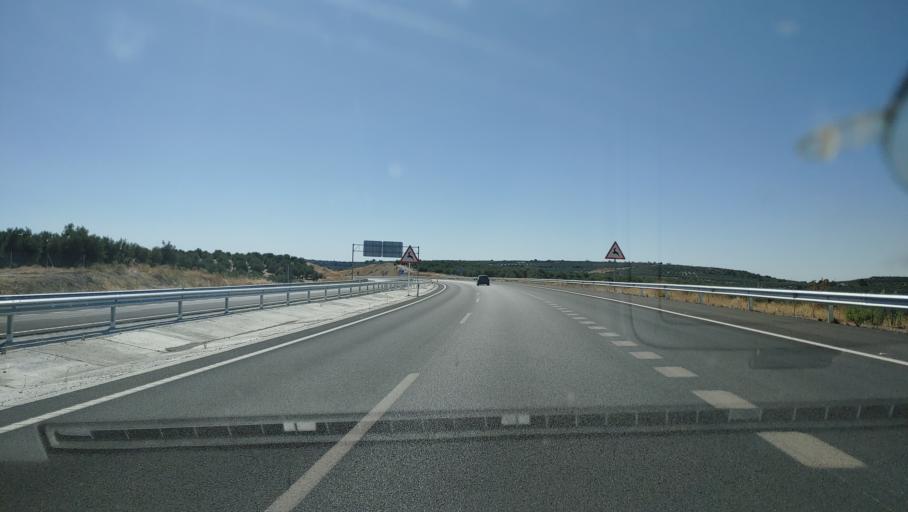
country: ES
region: Andalusia
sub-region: Provincia de Jaen
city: Torreperogil
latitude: 38.0501
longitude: -3.3019
